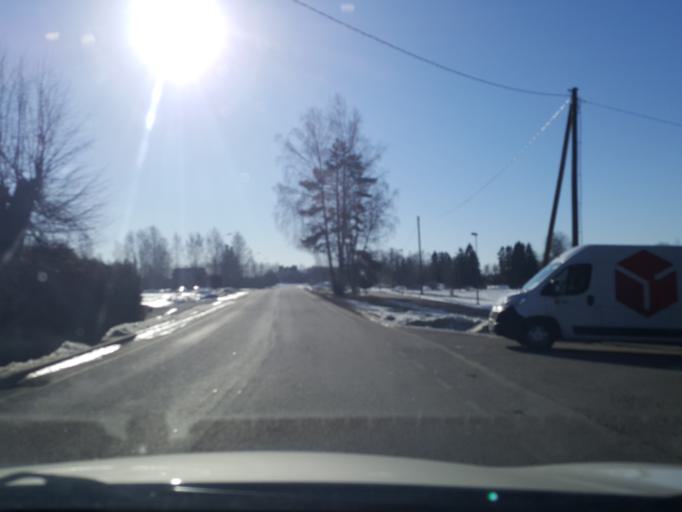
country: EE
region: Viljandimaa
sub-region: Viiratsi vald
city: Viiratsi
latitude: 58.4310
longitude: 25.6839
